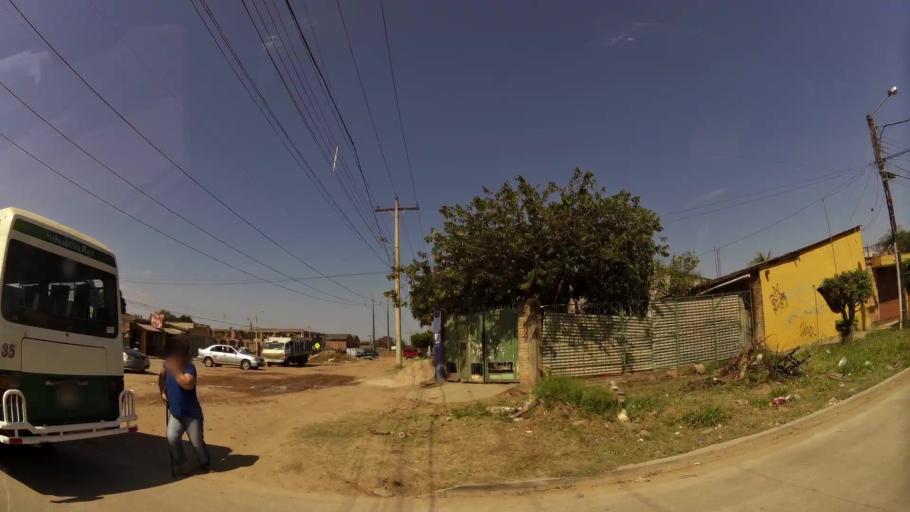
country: BO
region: Santa Cruz
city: Santa Cruz de la Sierra
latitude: -17.7485
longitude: -63.1470
